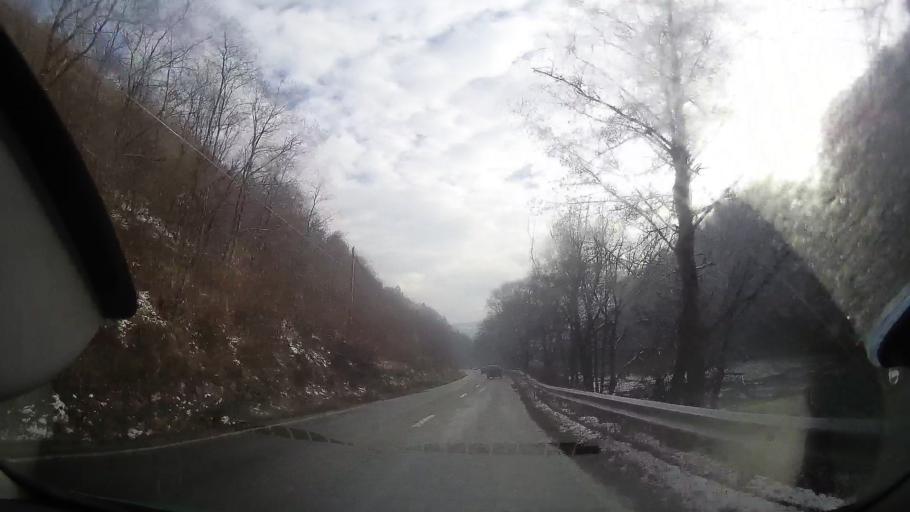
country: RO
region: Alba
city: Salciua de Sus
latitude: 46.3997
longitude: 23.3793
